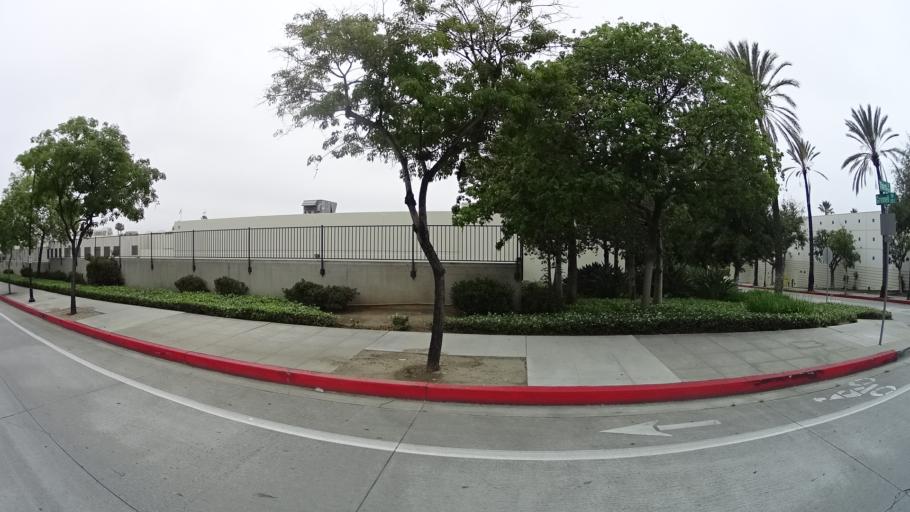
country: US
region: California
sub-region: Los Angeles County
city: Burbank
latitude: 34.1864
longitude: -118.3137
